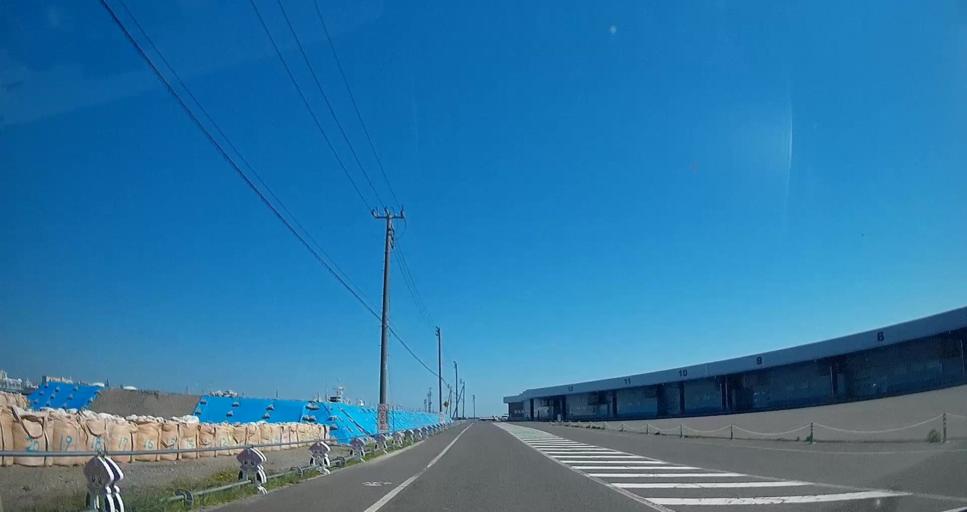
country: JP
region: Aomori
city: Hachinohe
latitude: 40.5272
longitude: 141.5361
